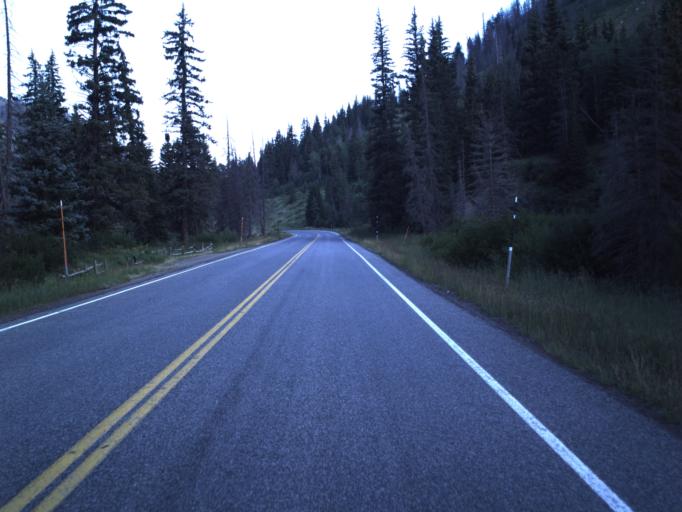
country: US
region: Utah
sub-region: Sanpete County
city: Fairview
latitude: 39.5521
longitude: -111.1701
